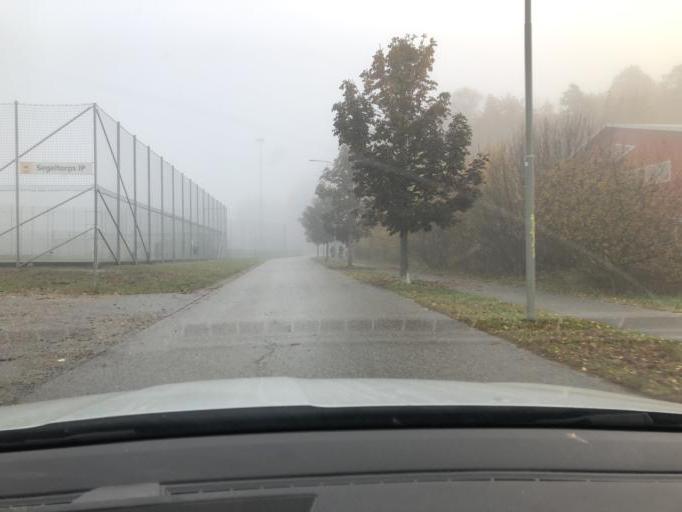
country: SE
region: Stockholm
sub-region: Huddinge Kommun
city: Segeltorp
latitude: 59.2656
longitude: 17.9288
